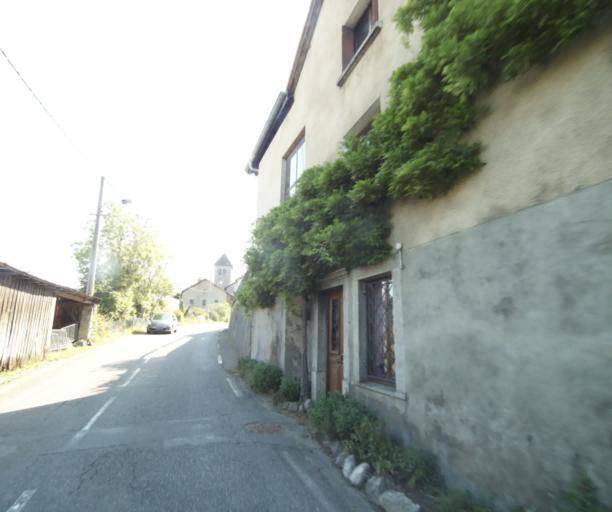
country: FR
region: Rhone-Alpes
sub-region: Departement de la Haute-Savoie
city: Allinges
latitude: 46.3121
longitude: 6.4892
